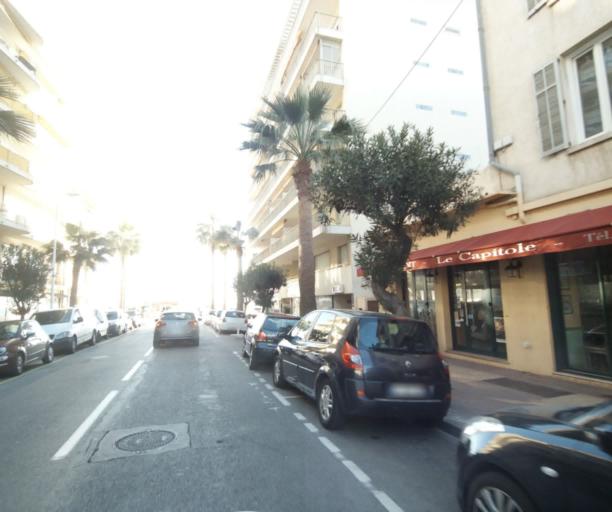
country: FR
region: Provence-Alpes-Cote d'Azur
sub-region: Departement des Alpes-Maritimes
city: Antibes
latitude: 43.5696
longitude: 7.1086
